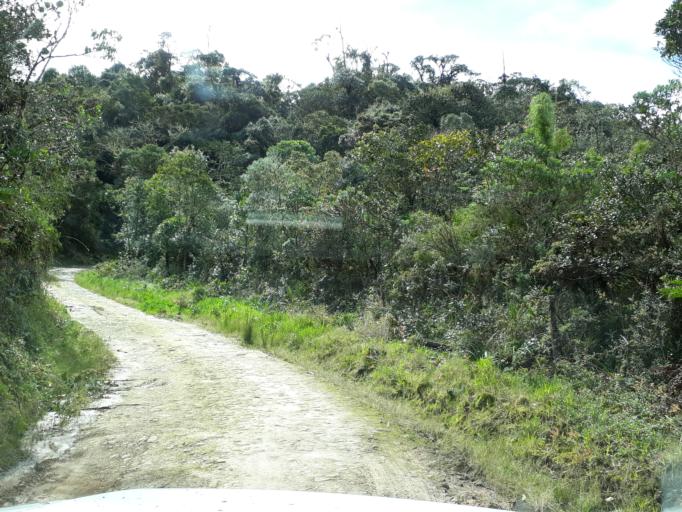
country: CO
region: Cundinamarca
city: Junin
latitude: 4.7872
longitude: -73.7747
